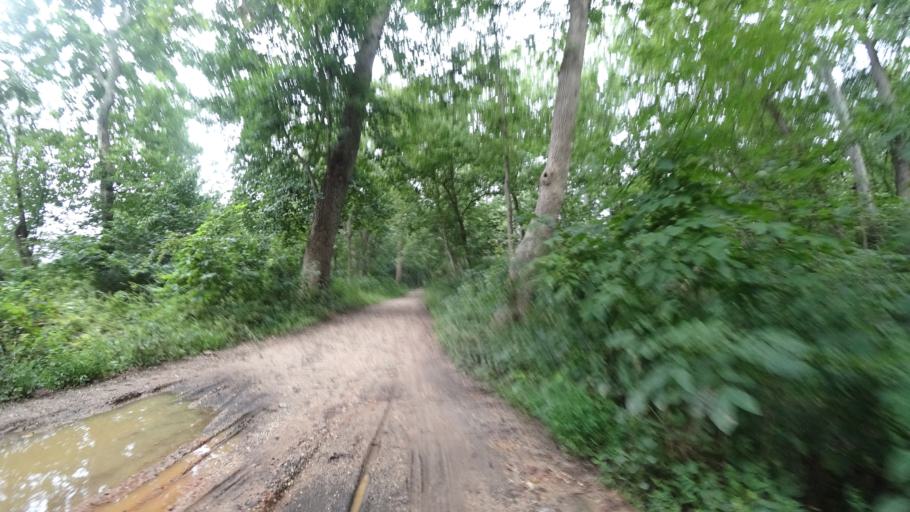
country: US
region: Virginia
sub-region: Loudoun County
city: Lowes Island
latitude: 39.0673
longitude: -77.3701
